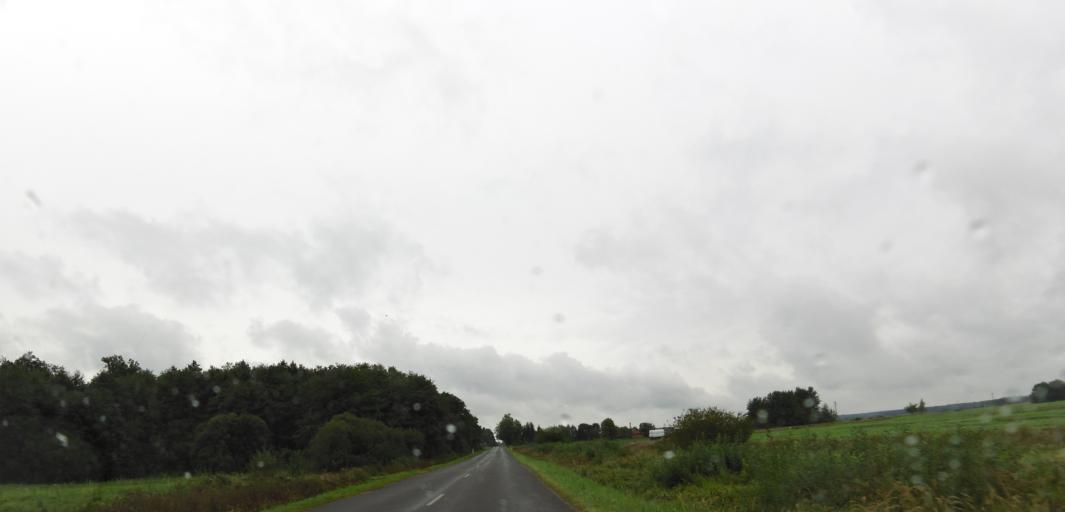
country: LT
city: Sirvintos
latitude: 55.0716
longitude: 24.9664
